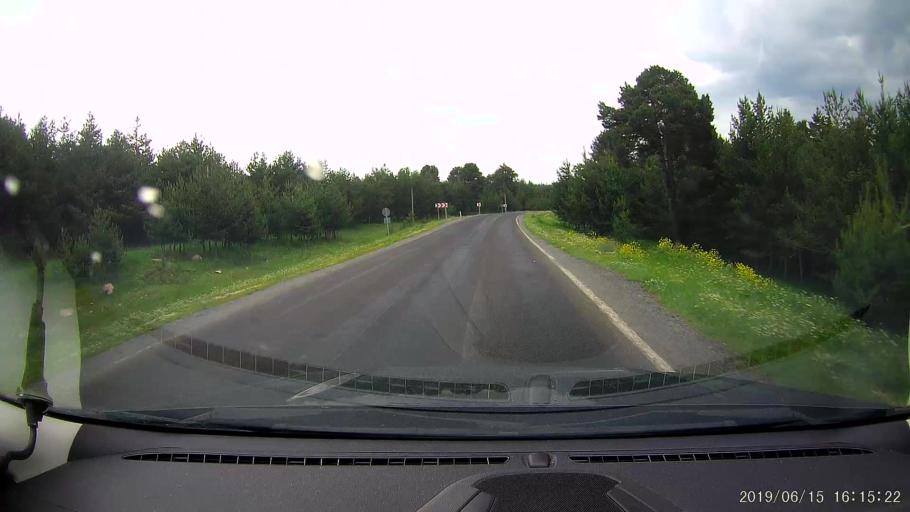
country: TR
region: Ardahan
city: Hanak
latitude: 41.2692
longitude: 42.8557
